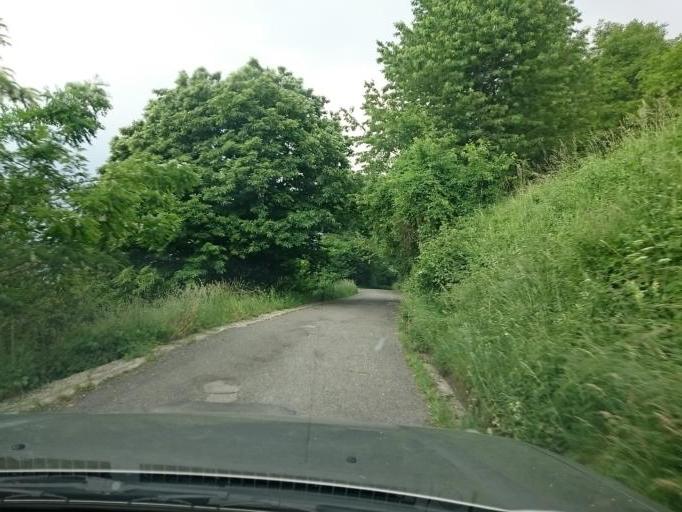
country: IT
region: Lombardy
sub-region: Provincia di Brescia
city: Paspardo
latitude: 46.0350
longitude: 10.3698
